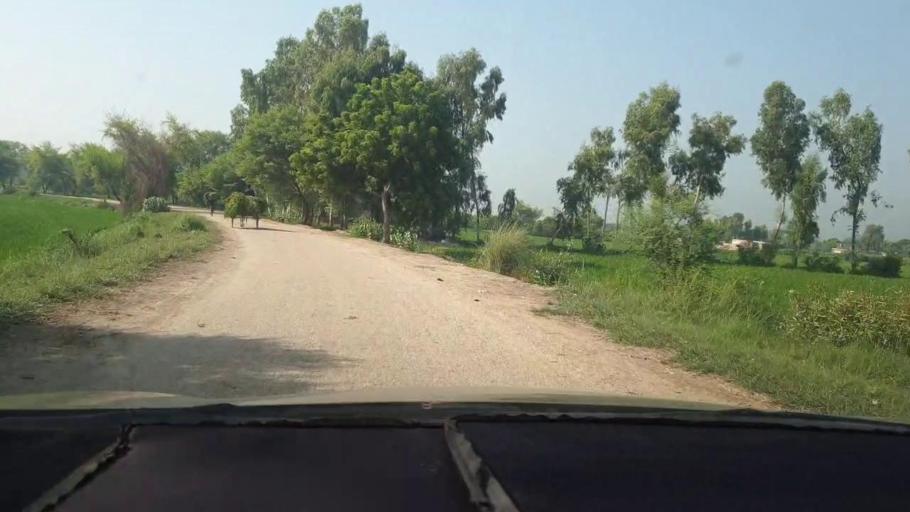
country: PK
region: Sindh
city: Kambar
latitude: 27.6122
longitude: 68.0907
